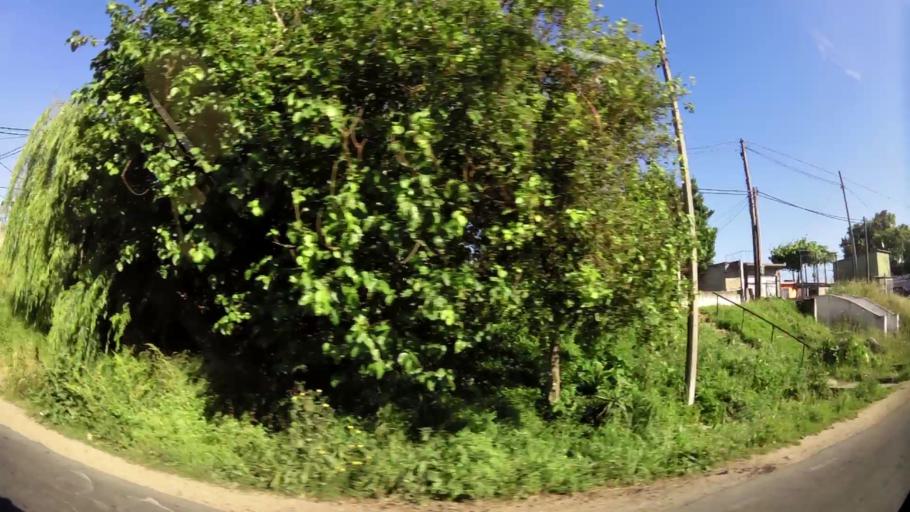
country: UY
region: Canelones
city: La Paz
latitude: -34.8143
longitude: -56.1700
